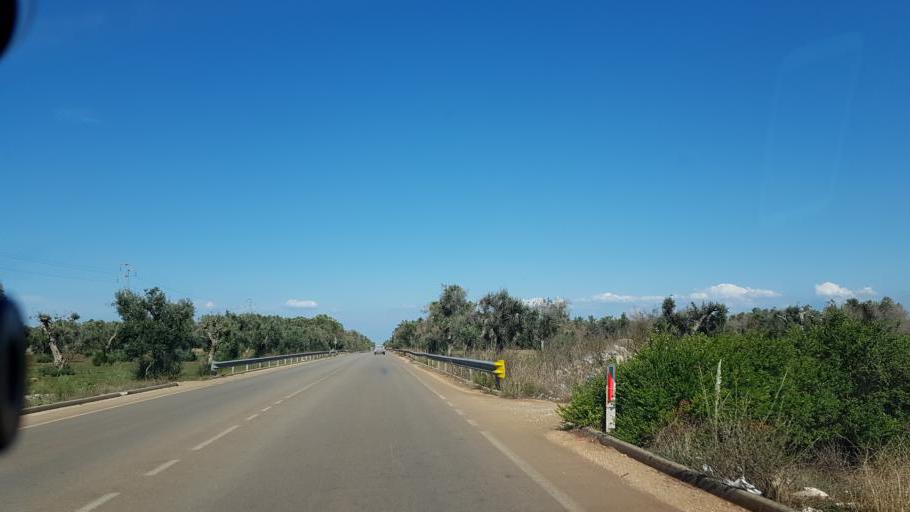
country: IT
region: Apulia
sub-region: Provincia di Lecce
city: Leverano
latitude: 40.2468
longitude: 17.9792
